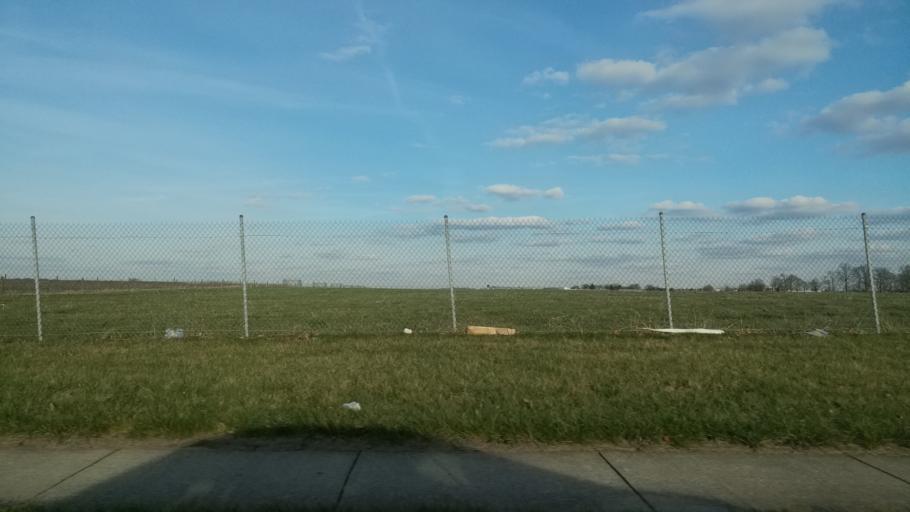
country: US
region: Ohio
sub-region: Franklin County
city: Dublin
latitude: 40.0764
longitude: -83.0925
